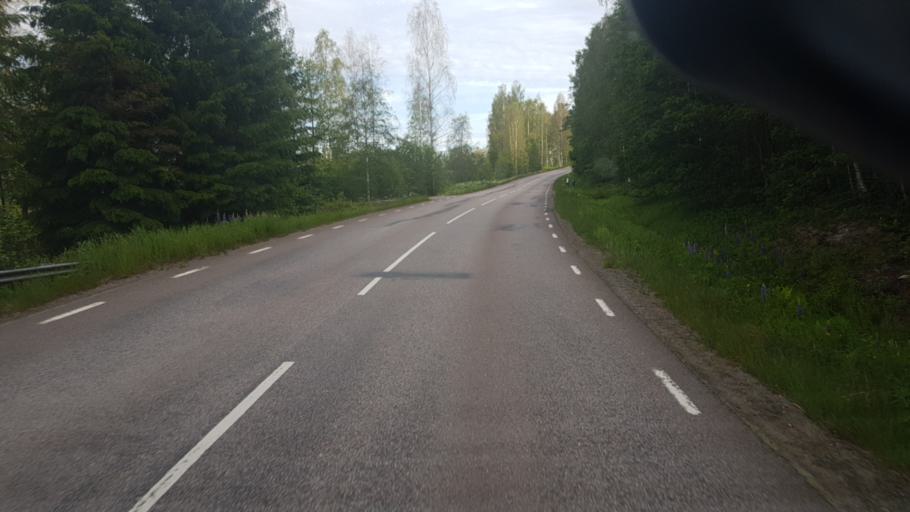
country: SE
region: Vaermland
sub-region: Arvika Kommun
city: Arvika
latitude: 59.7639
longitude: 12.6131
